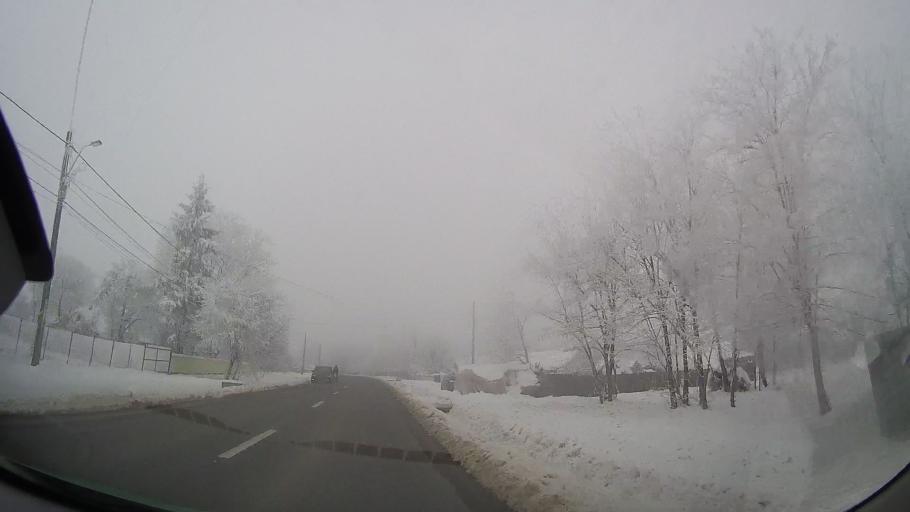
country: RO
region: Iasi
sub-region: Comuna Mogosesti-Siret
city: Mogosesti-Siret
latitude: 47.1637
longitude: 26.7710
